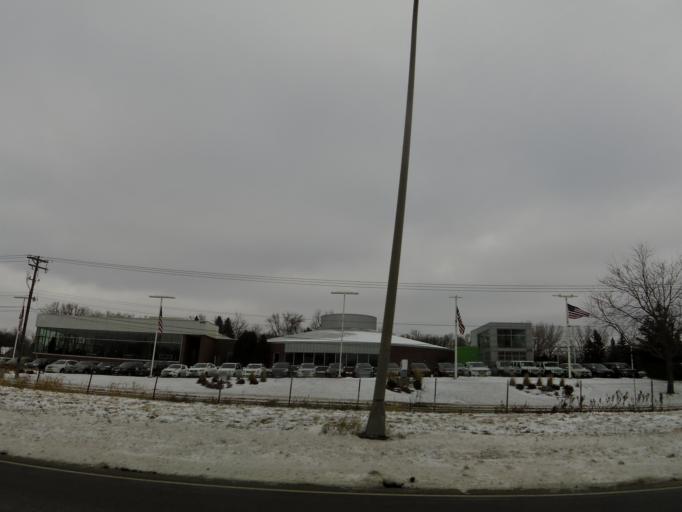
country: US
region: Minnesota
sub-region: Hennepin County
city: Minnetonka Mills
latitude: 44.9712
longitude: -93.4523
